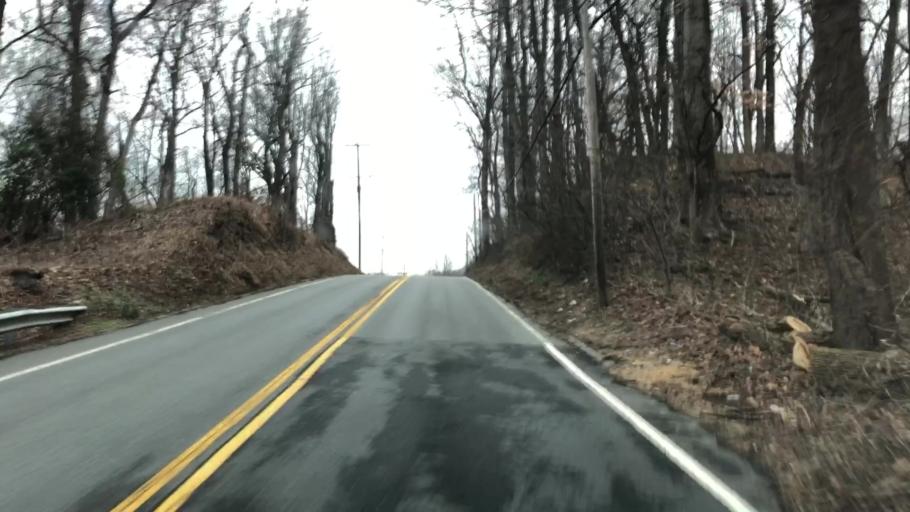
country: US
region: Maryland
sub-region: Calvert County
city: Chesapeake Beach
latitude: 38.6749
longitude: -76.5345
